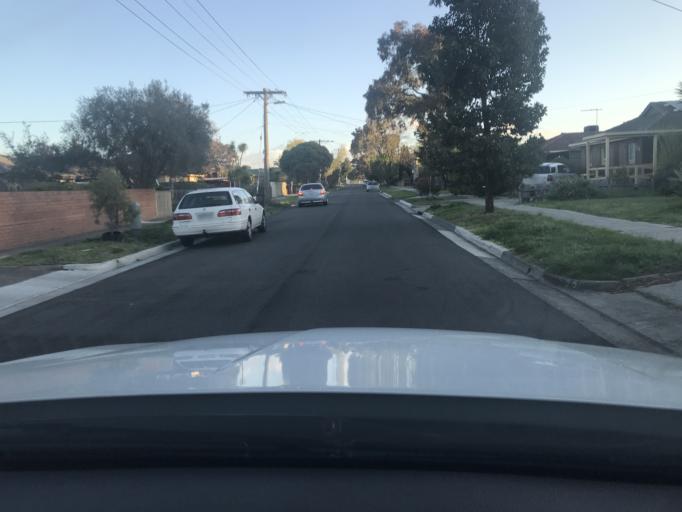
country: AU
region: Victoria
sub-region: Hume
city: Craigieburn
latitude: -37.5939
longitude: 144.9351
